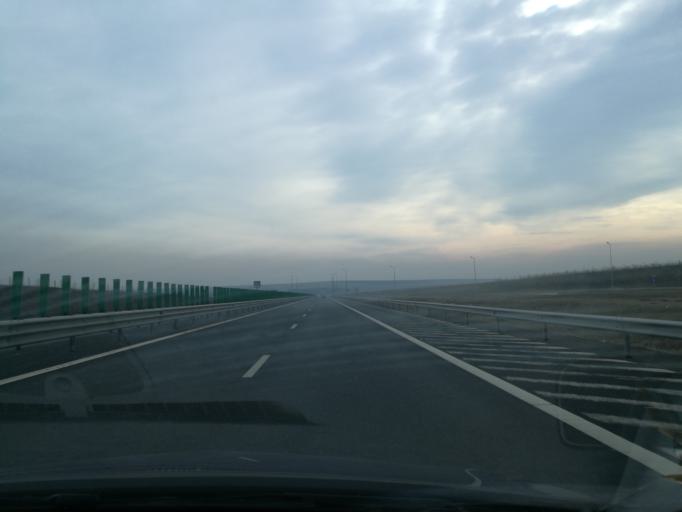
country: RO
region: Constanta
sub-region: Oras Murfatlar
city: Siminoc
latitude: 44.1487
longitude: 28.3584
